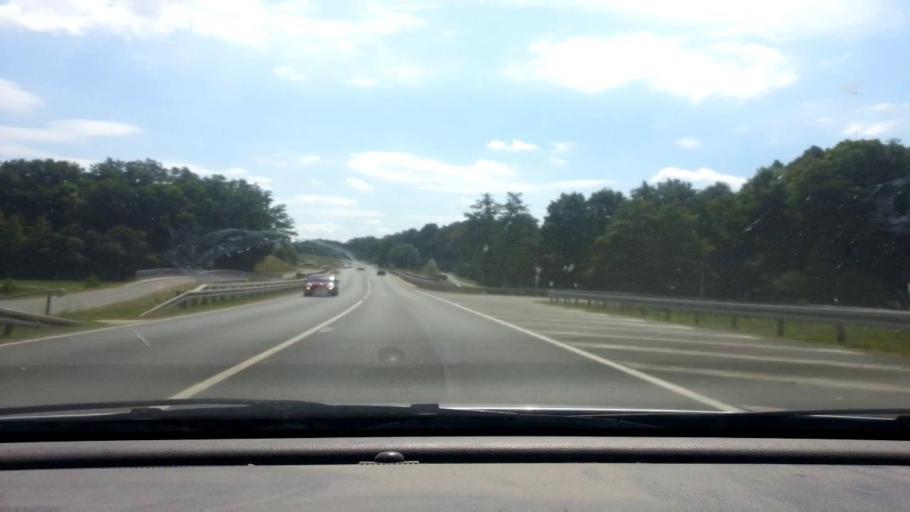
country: DE
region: Bavaria
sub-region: Upper Franconia
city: Neunkirchen am Main
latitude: 49.9216
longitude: 11.6370
